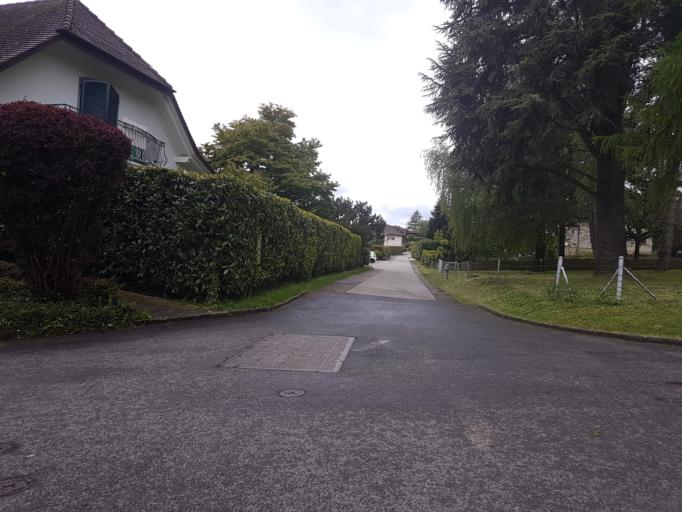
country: CH
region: Vaud
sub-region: Ouest Lausannois District
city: Ecublens
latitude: 46.5350
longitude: 6.5436
